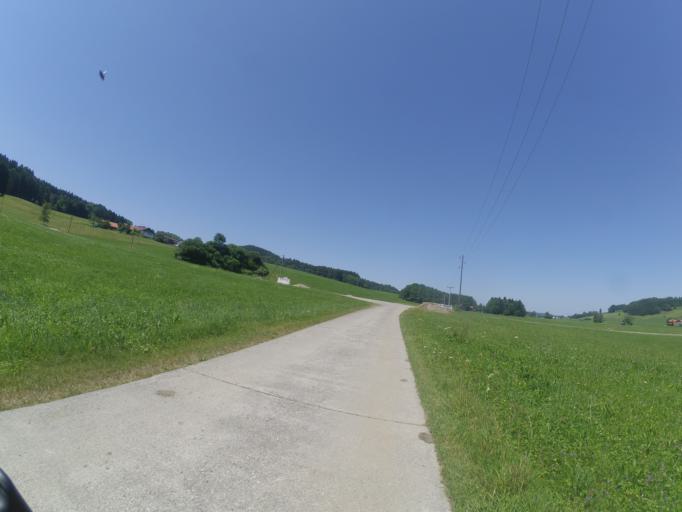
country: DE
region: Bavaria
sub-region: Swabia
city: Bohen
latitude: 47.8704
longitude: 10.3376
